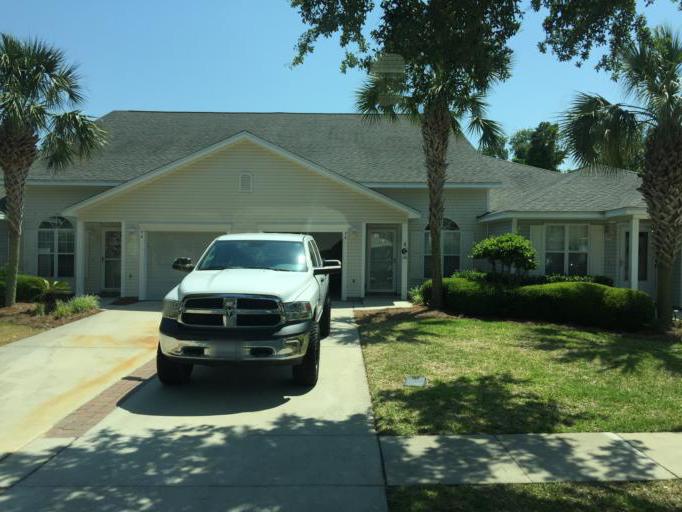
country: US
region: Florida
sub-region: Bay County
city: Laguna Beach
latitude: 30.2203
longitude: -85.8585
